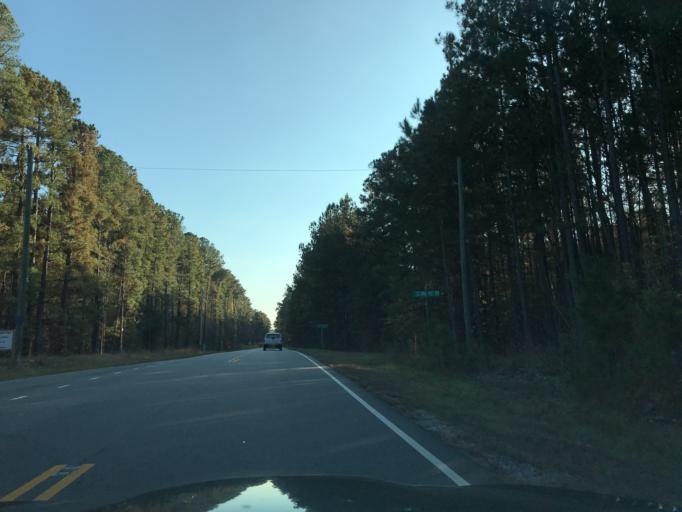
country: US
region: North Carolina
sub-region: Granville County
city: Creedmoor
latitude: 36.0803
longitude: -78.6926
